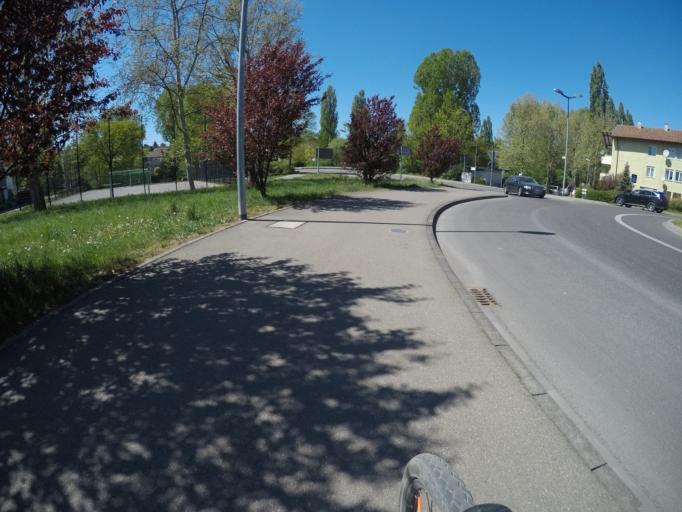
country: DE
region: Baden-Wuerttemberg
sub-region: Regierungsbezirk Stuttgart
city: Waiblingen
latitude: 48.8371
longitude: 9.3152
